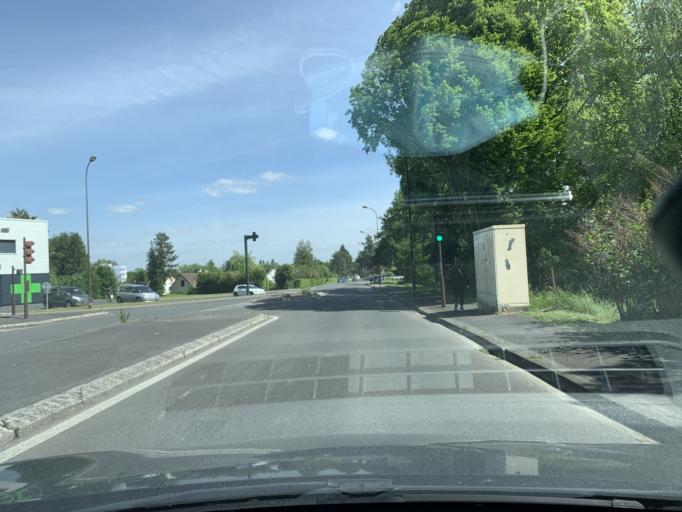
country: FR
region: Picardie
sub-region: Departement de l'Aisne
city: Saint-Quentin
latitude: 49.8582
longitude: 3.3043
